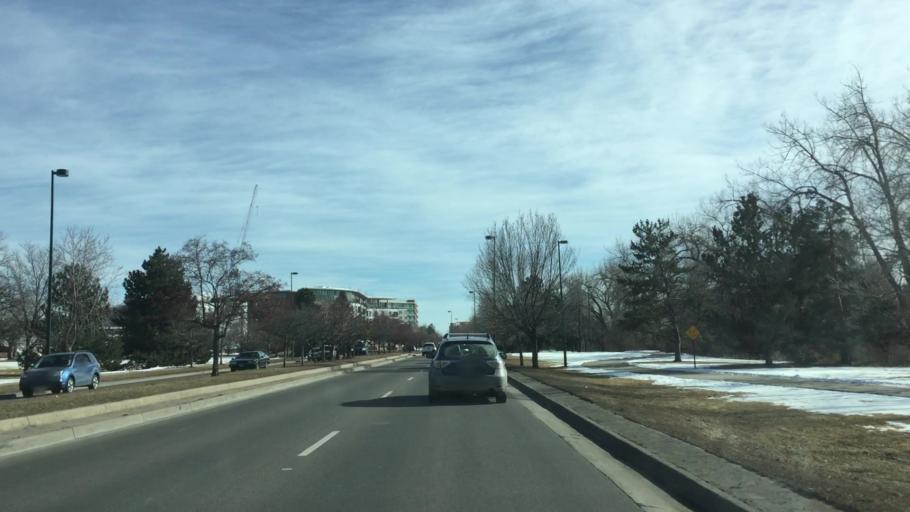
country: US
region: Colorado
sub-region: Arapahoe County
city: Glendale
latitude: 39.7132
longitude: -104.9492
